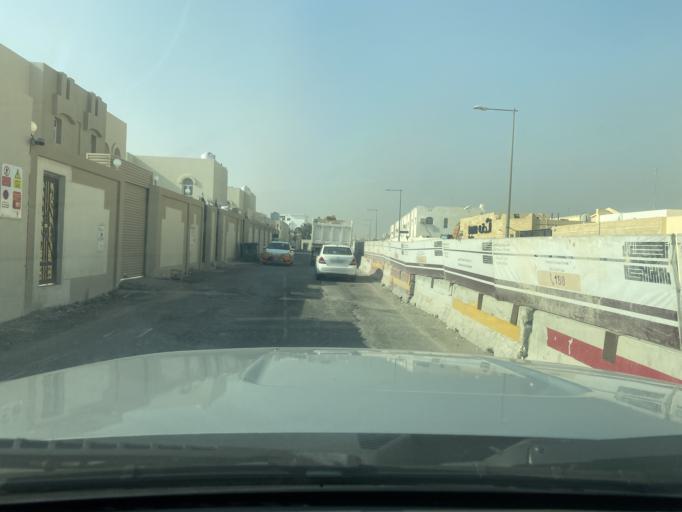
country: QA
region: Baladiyat ad Dawhah
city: Doha
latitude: 25.2390
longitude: 51.5702
